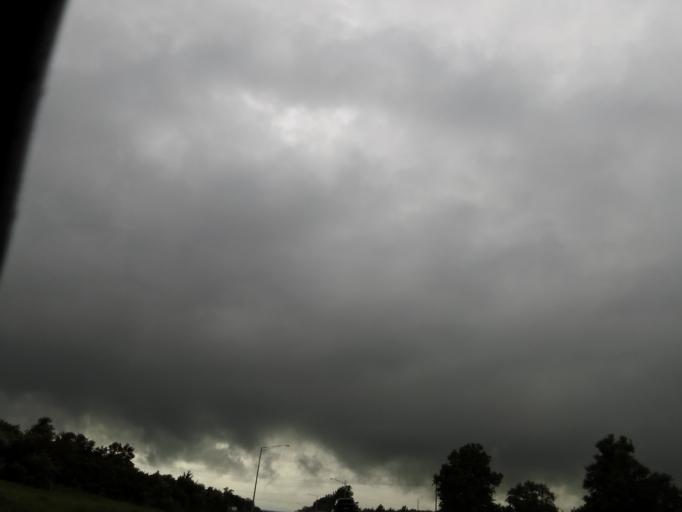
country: US
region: Illinois
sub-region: Jefferson County
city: Mount Vernon
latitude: 38.3373
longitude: -88.9574
